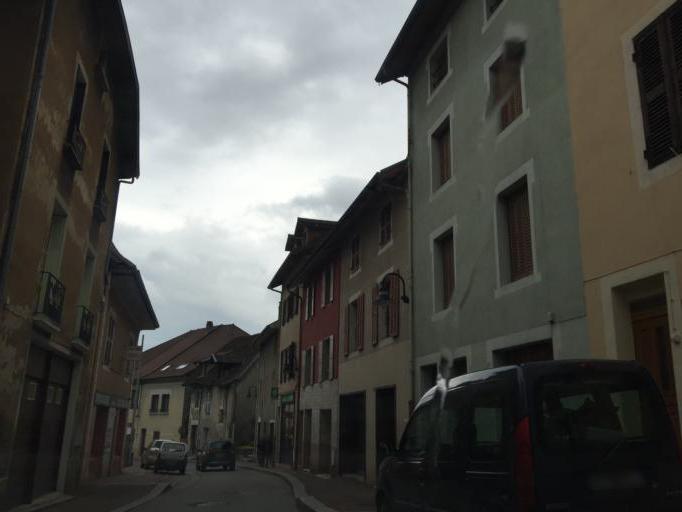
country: FR
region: Rhone-Alpes
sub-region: Departement de la Savoie
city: Les Echelles
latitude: 45.4368
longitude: 5.7540
